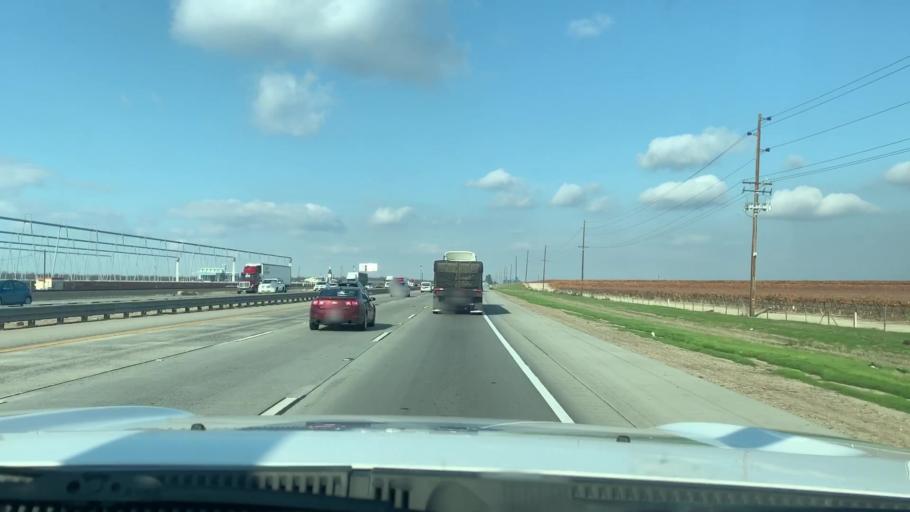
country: US
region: California
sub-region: Kern County
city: Shafter
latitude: 35.5663
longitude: -119.1998
